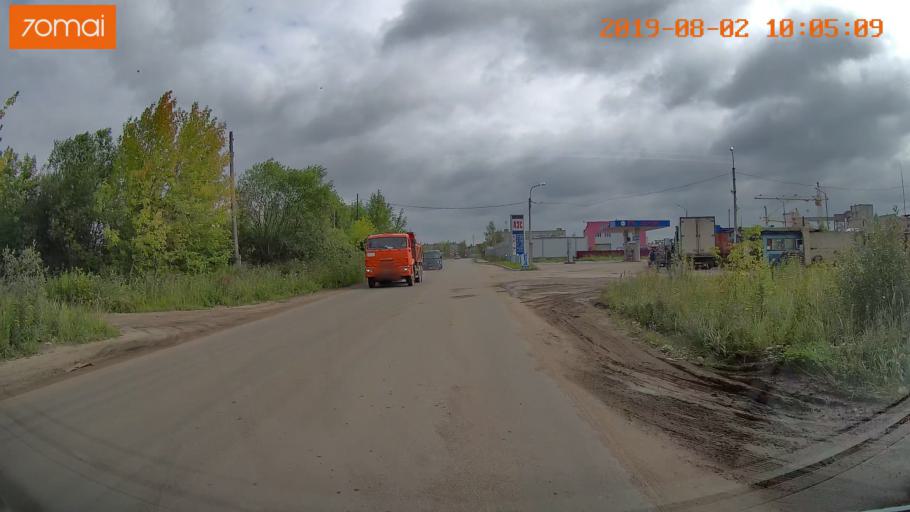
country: RU
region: Ivanovo
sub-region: Gorod Ivanovo
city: Ivanovo
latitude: 56.9769
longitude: 40.9231
